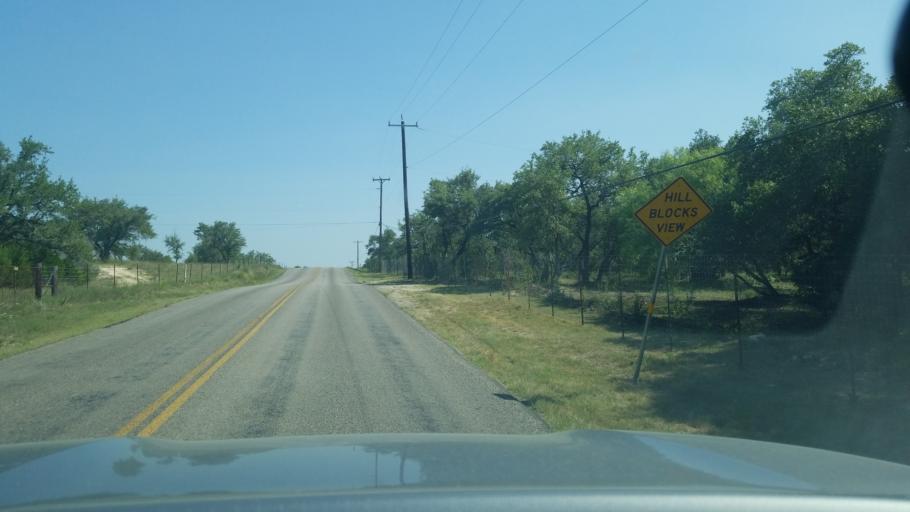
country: US
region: Texas
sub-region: Comal County
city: Bulverde
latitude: 29.7571
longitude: -98.5128
